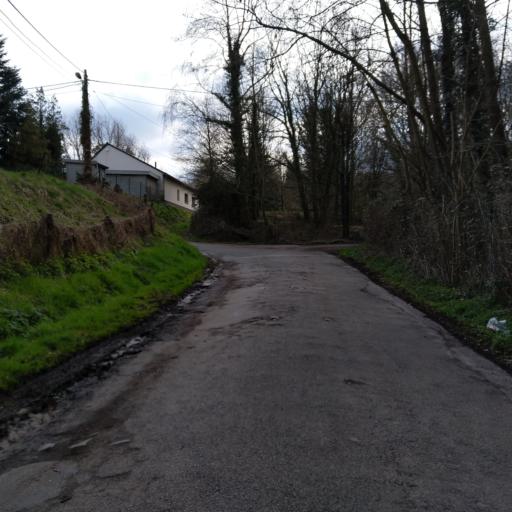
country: BE
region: Wallonia
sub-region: Province du Hainaut
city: Mons
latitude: 50.5119
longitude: 3.9923
